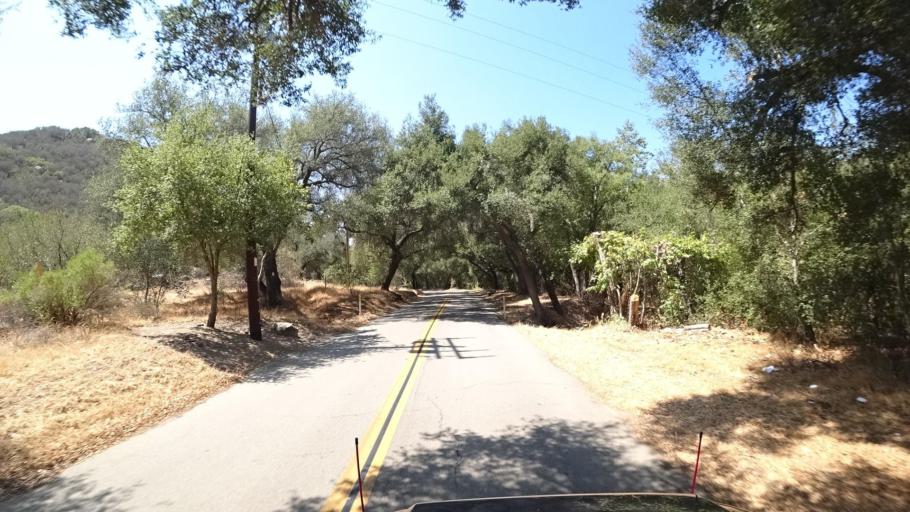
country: US
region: California
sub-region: San Diego County
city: Fallbrook
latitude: 33.4575
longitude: -117.2946
